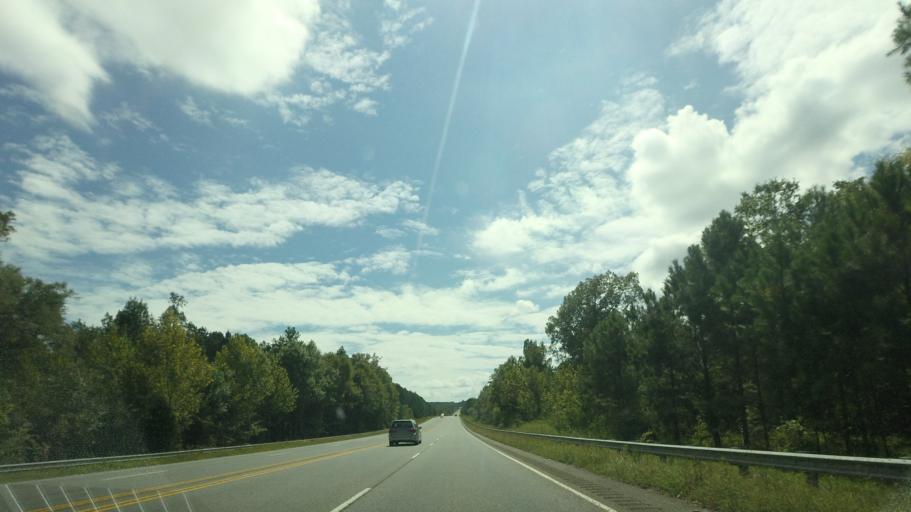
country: US
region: Georgia
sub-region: Bleckley County
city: Cochran
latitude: 32.5179
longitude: -83.4310
